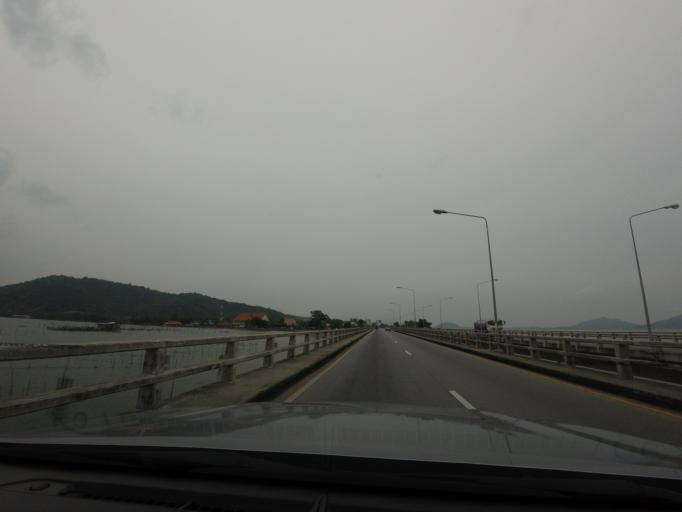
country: TH
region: Songkhla
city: Ban Mai
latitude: 7.1558
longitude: 100.5585
